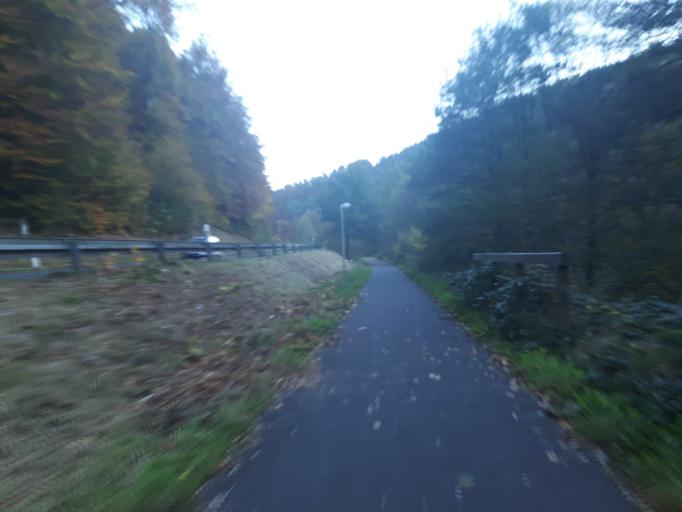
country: DE
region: Bavaria
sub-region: Regierungsbezirk Unterfranken
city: Heimbuchenthal
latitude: 49.9022
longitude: 9.2997
